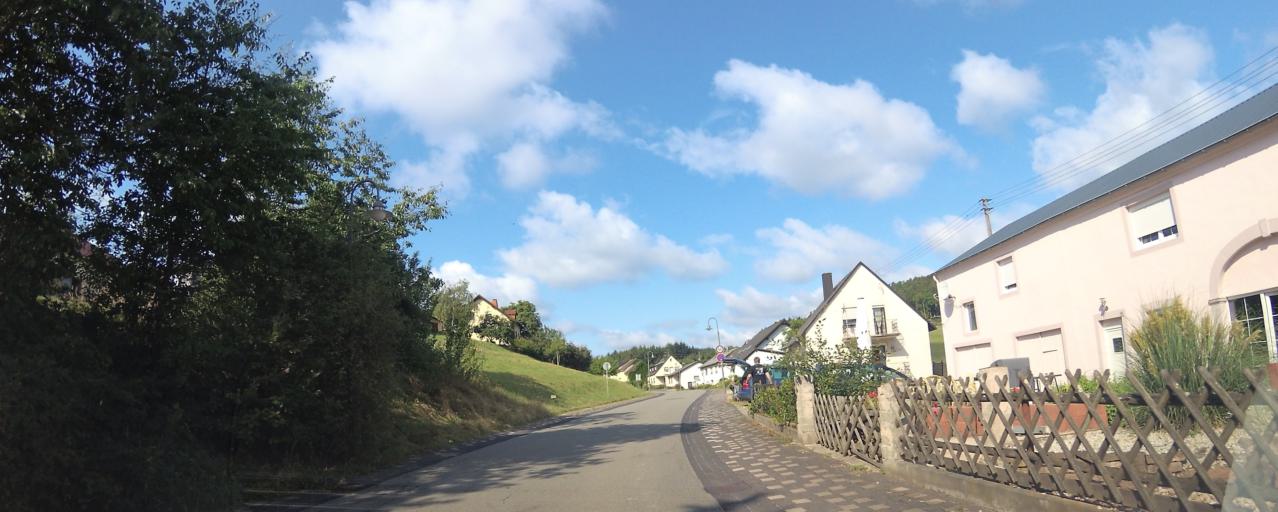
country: DE
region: Rheinland-Pfalz
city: Dierscheid
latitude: 49.8804
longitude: 6.7480
